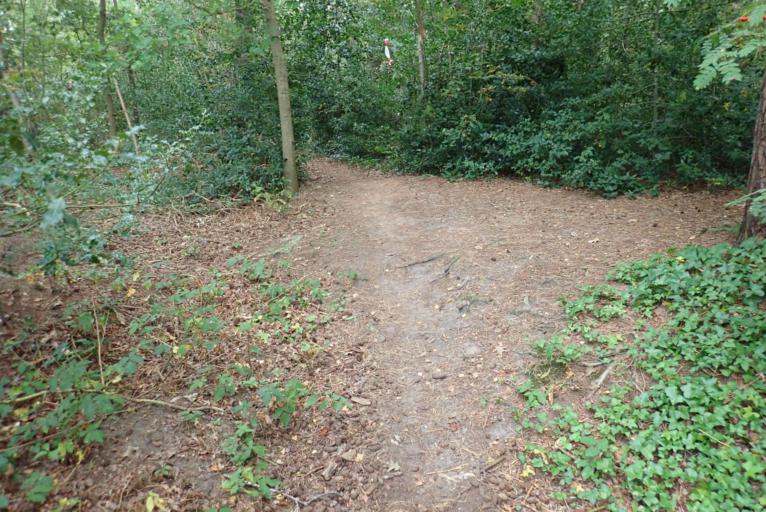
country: BE
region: Flanders
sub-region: Provincie Antwerpen
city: Essen
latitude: 51.4293
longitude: 4.4530
